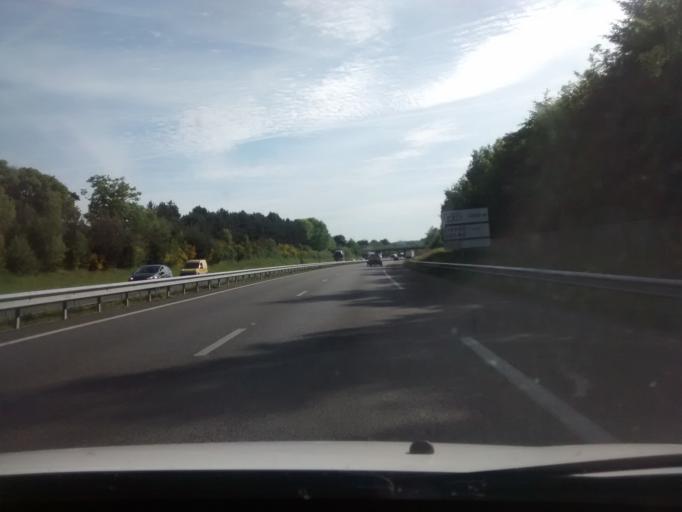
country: FR
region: Brittany
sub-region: Departement d'Ille-et-Vilaine
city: Liffre
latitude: 48.2148
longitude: -1.5164
